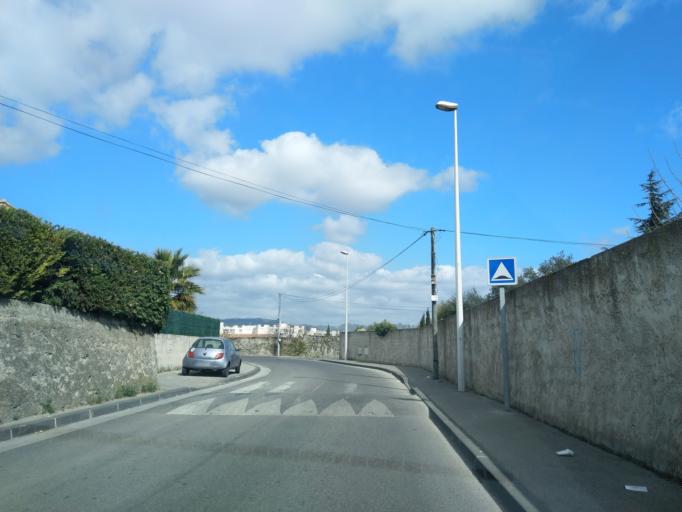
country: FR
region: Provence-Alpes-Cote d'Azur
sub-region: Departement des Bouches-du-Rhone
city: Plan-de-Cuques
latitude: 43.3269
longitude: 5.4552
